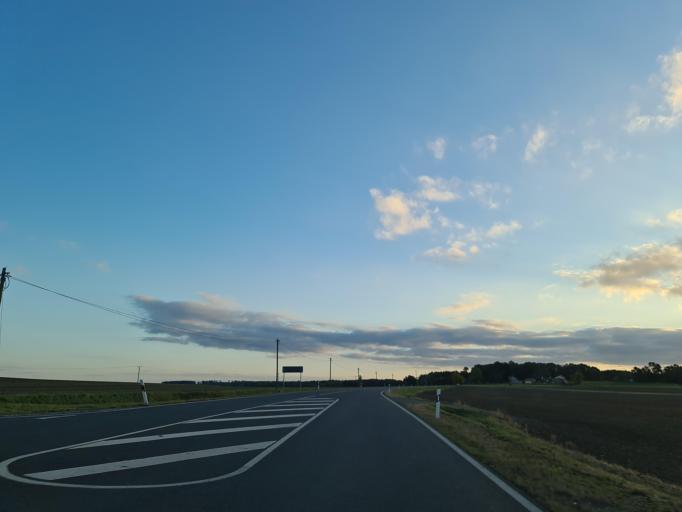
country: DE
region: Saxony
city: Syrau
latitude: 50.5593
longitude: 12.1239
